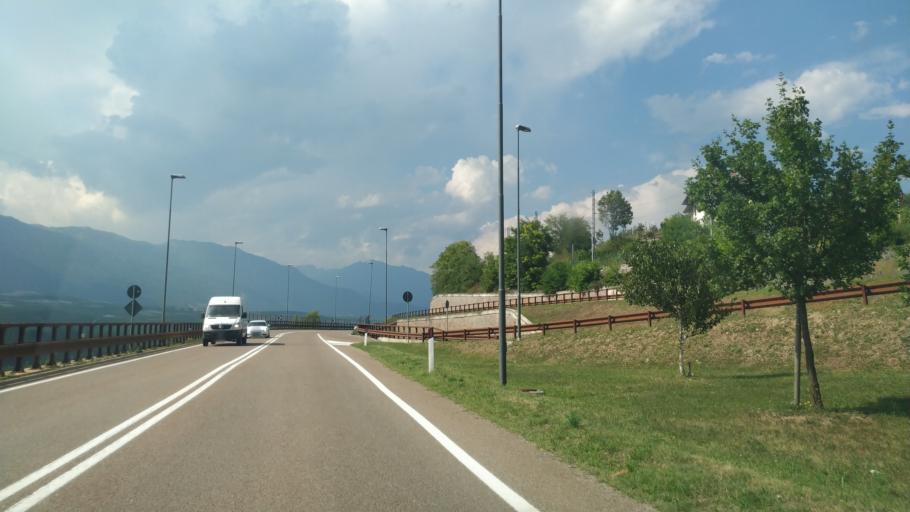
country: IT
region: Trentino-Alto Adige
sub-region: Provincia di Trento
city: Taio
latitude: 46.3066
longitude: 11.0700
